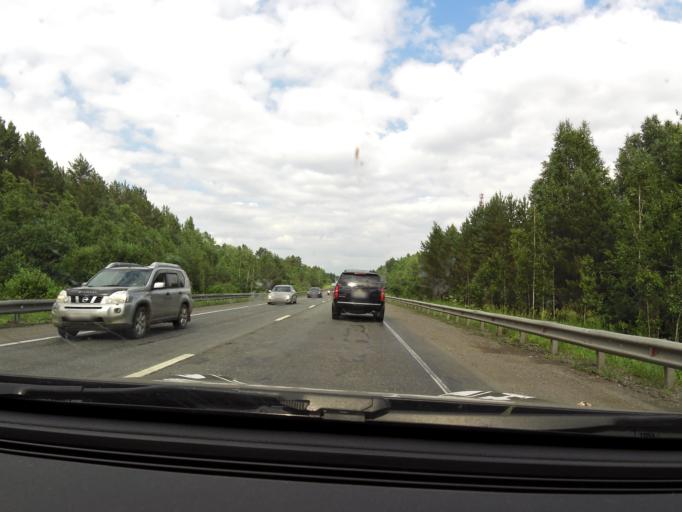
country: RU
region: Sverdlovsk
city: Druzhinino
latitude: 56.8020
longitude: 59.4747
